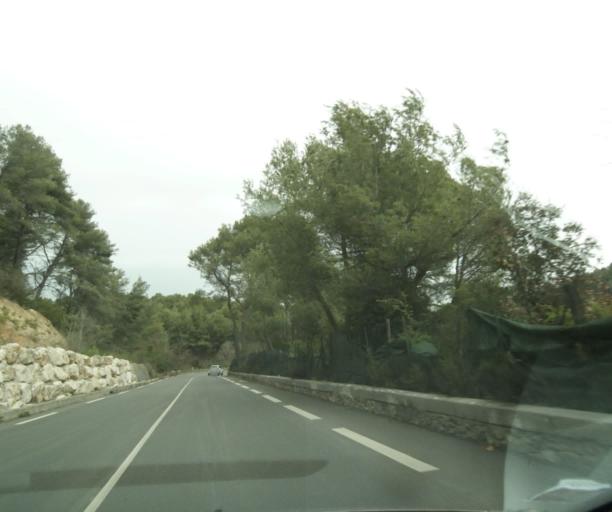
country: FR
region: Provence-Alpes-Cote d'Azur
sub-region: Departement des Bouches-du-Rhone
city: Aix-en-Provence
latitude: 43.5474
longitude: 5.4606
